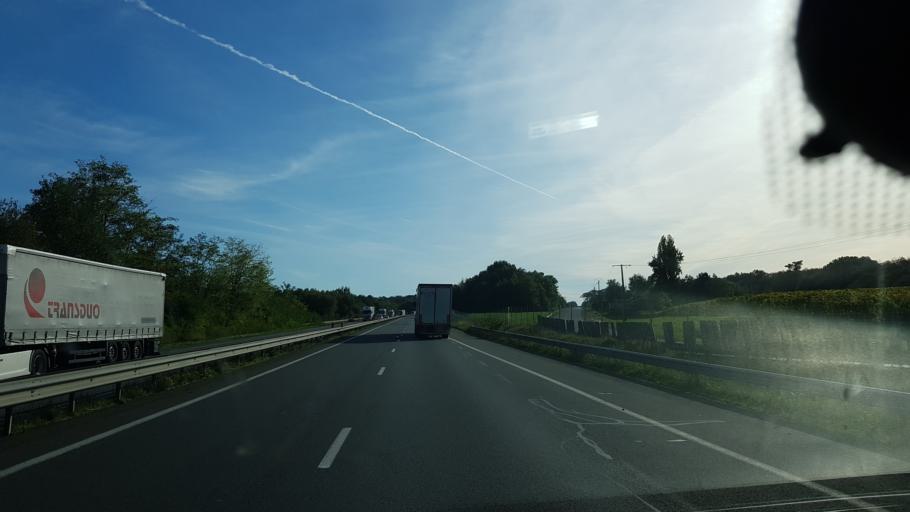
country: FR
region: Poitou-Charentes
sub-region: Departement de la Charente-Maritime
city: Chevanceaux
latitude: 45.2886
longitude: -0.2416
